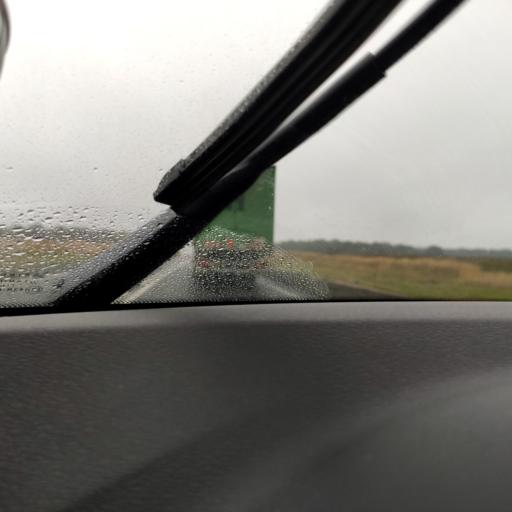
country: RU
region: Samara
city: Yelkhovka
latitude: 53.7095
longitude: 50.2286
